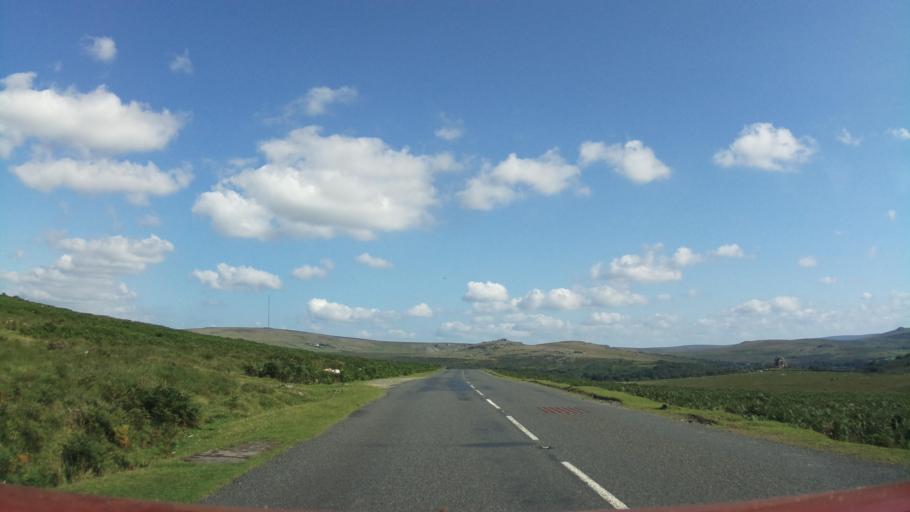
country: GB
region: England
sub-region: Devon
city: Horrabridge
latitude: 50.5572
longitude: -4.0686
